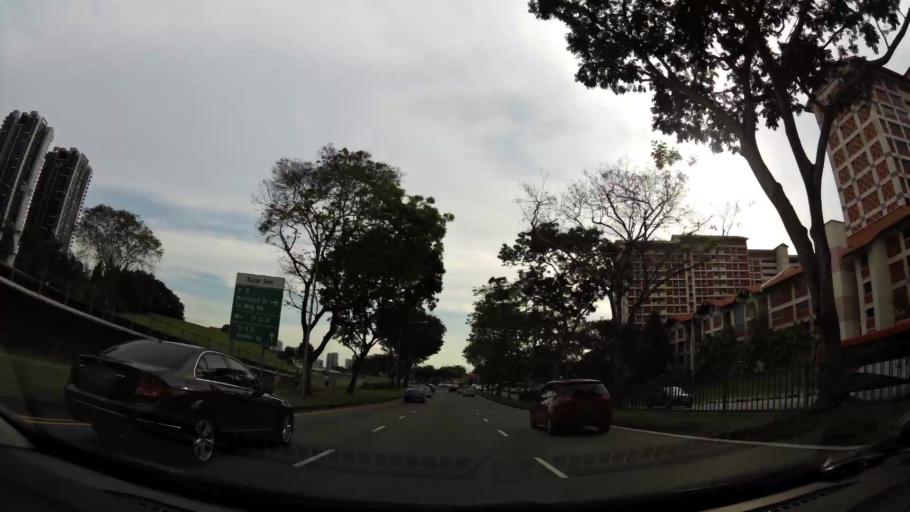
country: SG
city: Singapore
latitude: 1.3553
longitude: 103.8493
